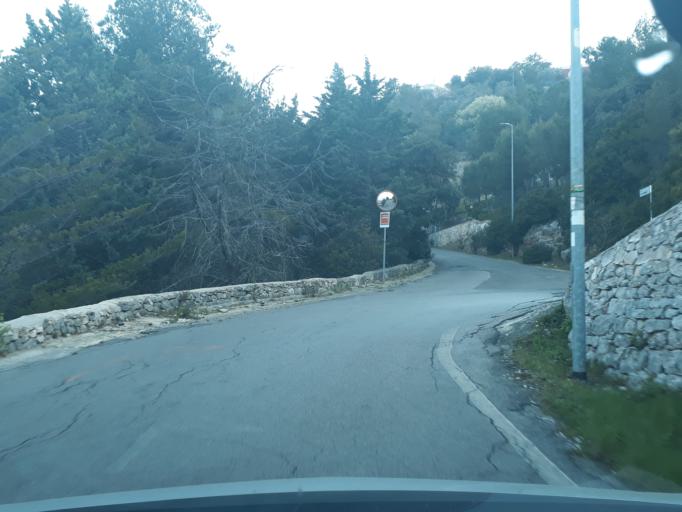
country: IT
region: Apulia
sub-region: Provincia di Brindisi
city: Lamie di Olimpie-Selva
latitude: 40.8295
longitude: 17.3376
